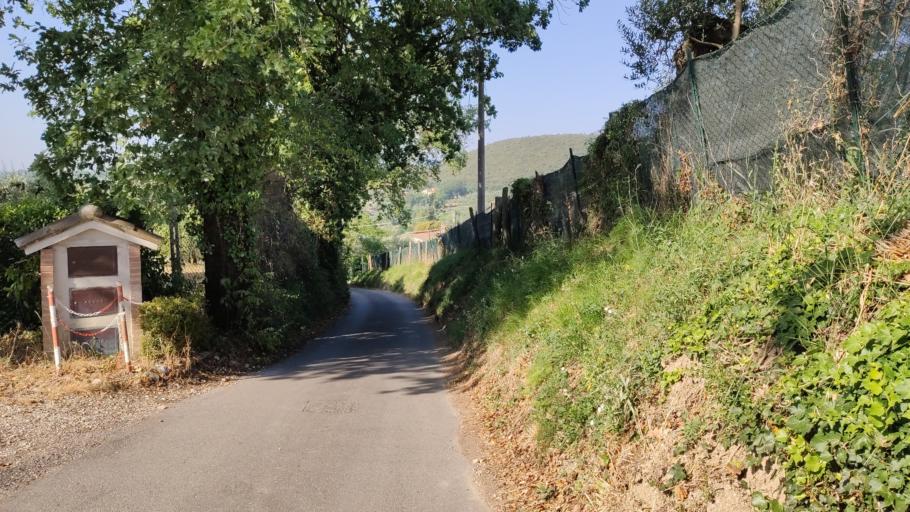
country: IT
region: Umbria
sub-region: Provincia di Terni
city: Amelia
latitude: 42.5363
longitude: 12.4112
